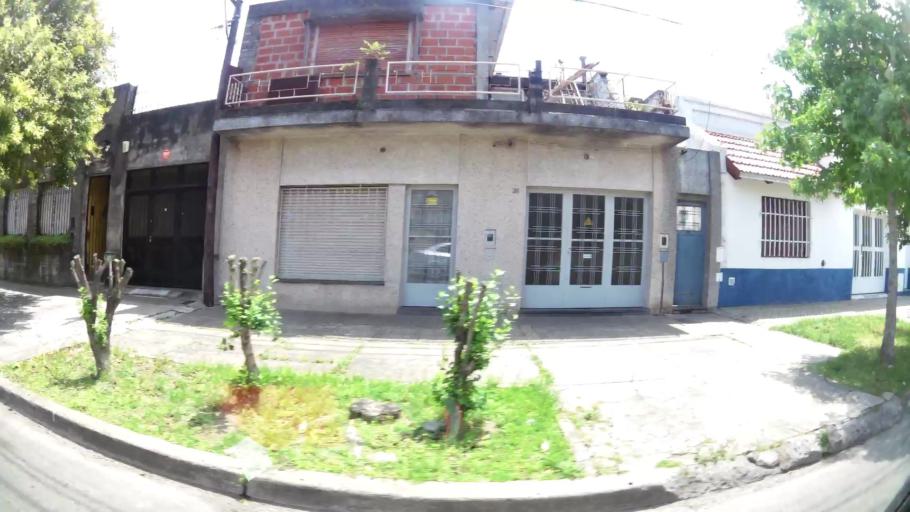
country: AR
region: Santa Fe
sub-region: Departamento de Rosario
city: Rosario
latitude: -32.9749
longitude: -60.6297
